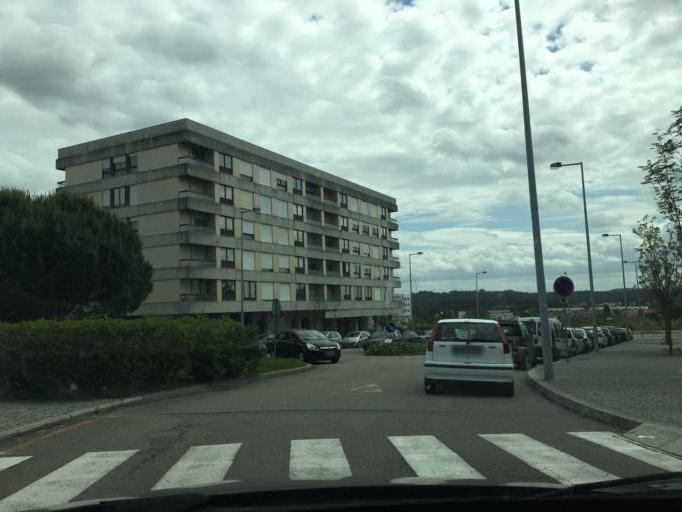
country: PT
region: Porto
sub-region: Maia
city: Anta
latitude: 41.2625
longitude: -8.6158
